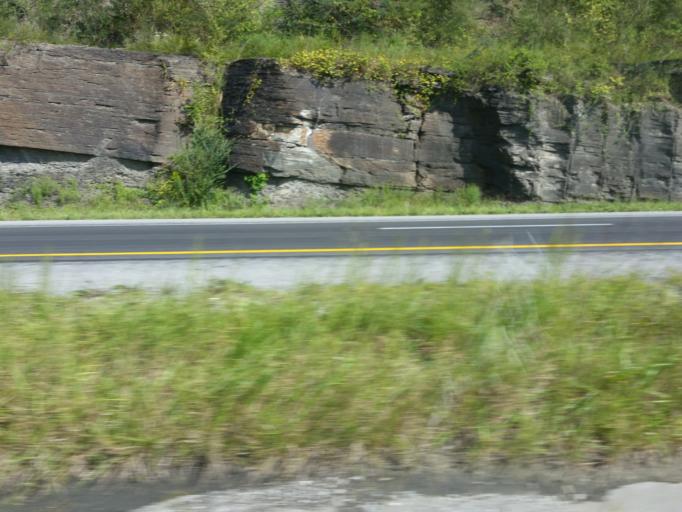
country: US
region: Kentucky
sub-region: Bell County
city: Pineville
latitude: 36.7379
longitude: -83.6962
